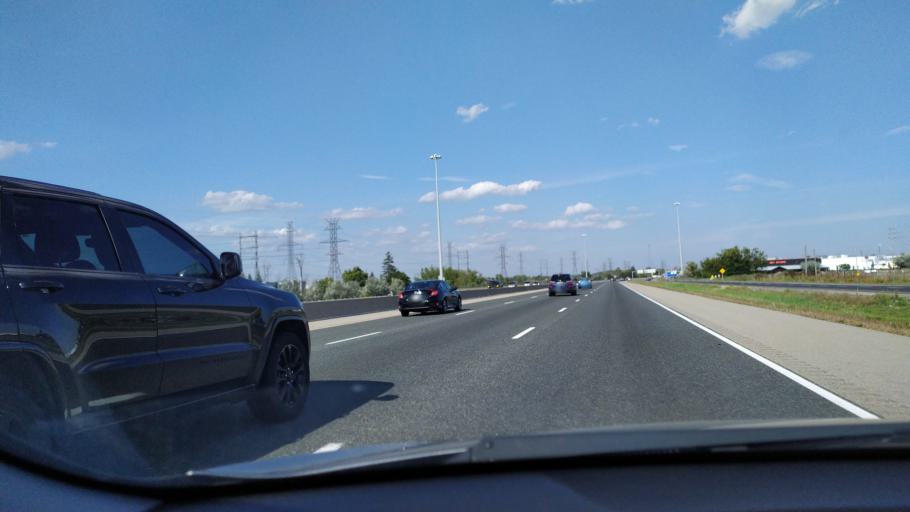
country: CA
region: Ontario
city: London
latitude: 42.9255
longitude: -81.2082
